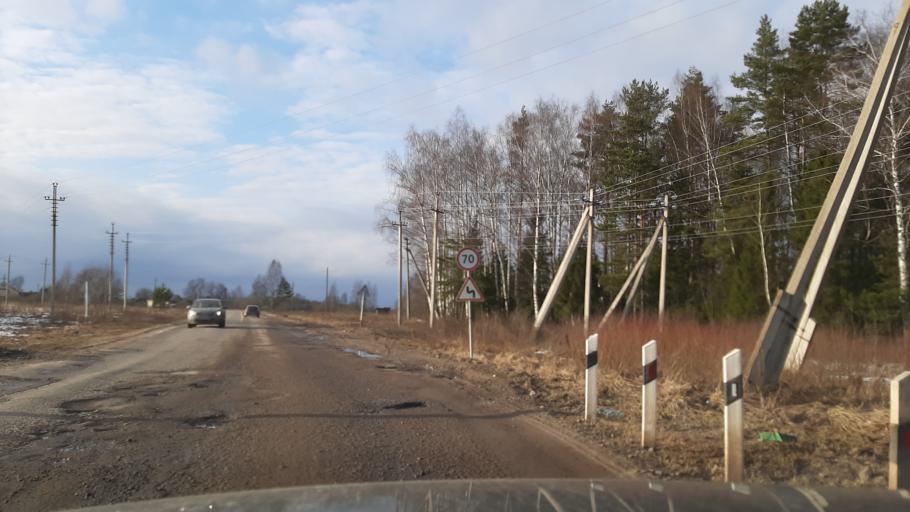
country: RU
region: Ivanovo
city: Novo-Talitsy
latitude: 56.9386
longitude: 40.7223
